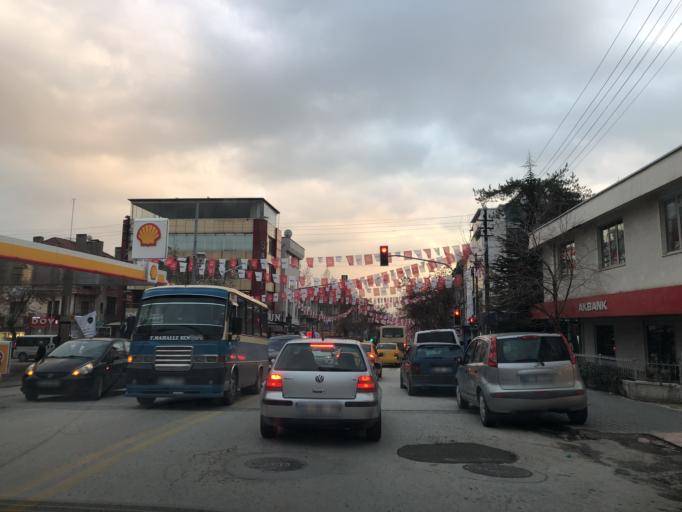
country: TR
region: Ankara
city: Ankara
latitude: 39.9666
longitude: 32.8085
